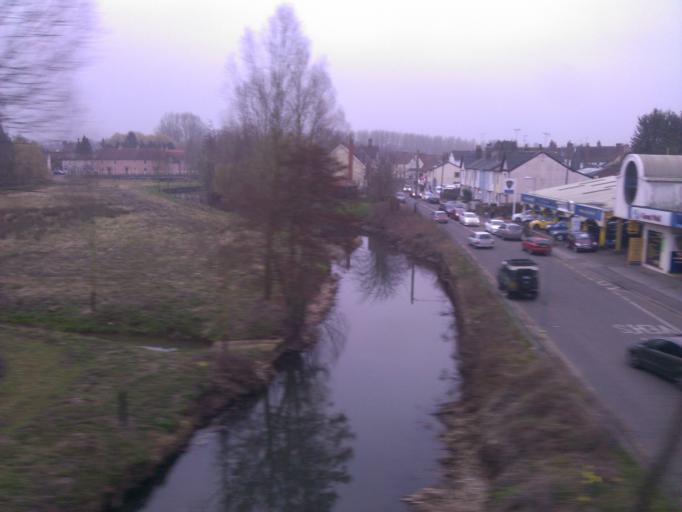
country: GB
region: England
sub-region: Essex
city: Kelvedon
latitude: 51.8416
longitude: 0.7042
